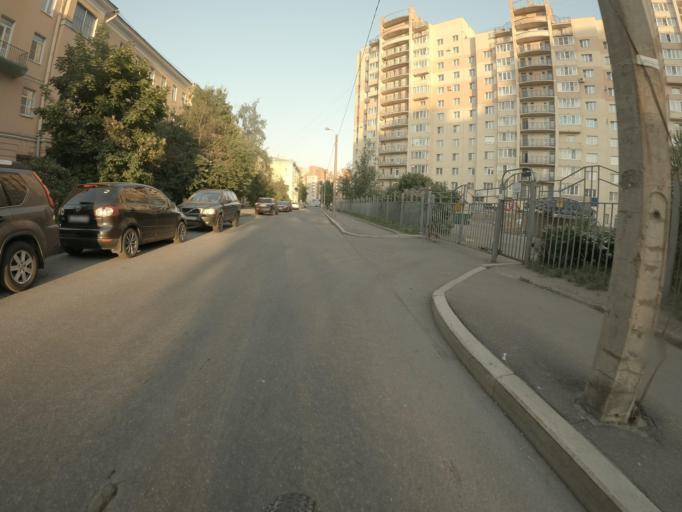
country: RU
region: St.-Petersburg
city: Dachnoye
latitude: 59.8530
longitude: 30.2454
